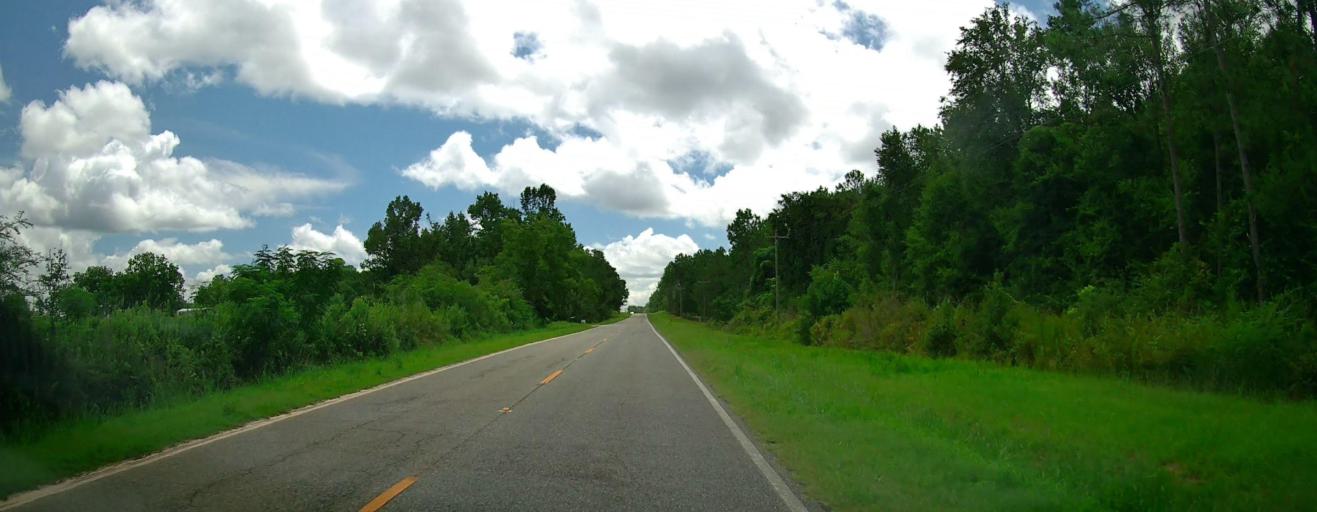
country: US
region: Georgia
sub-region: Wilcox County
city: Rochelle
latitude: 31.9073
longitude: -83.5532
